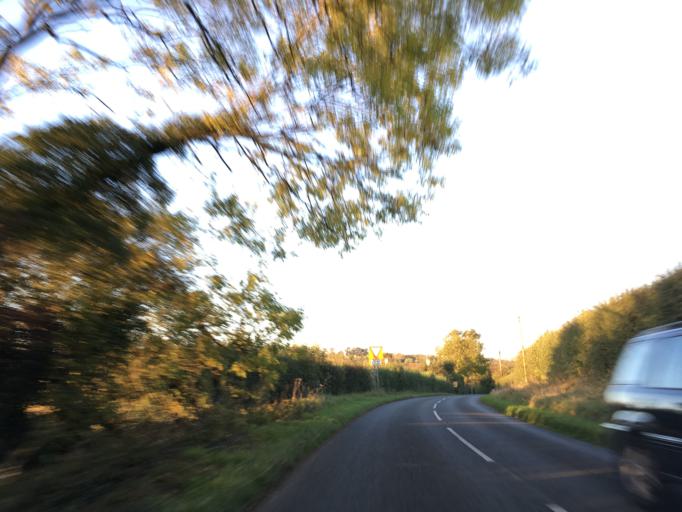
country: GB
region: England
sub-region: South Gloucestershire
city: Almondsbury
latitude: 51.5689
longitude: -2.5691
